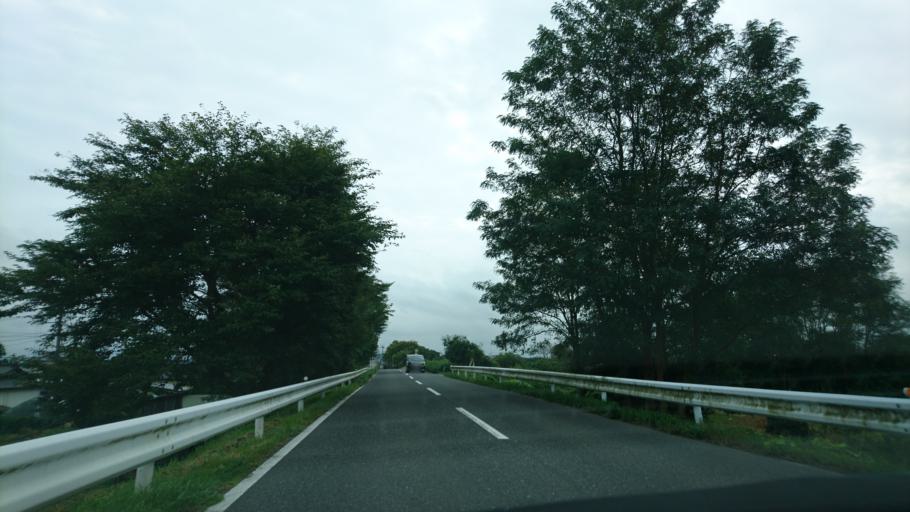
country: JP
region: Iwate
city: Ichinoseki
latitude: 38.7763
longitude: 141.1228
